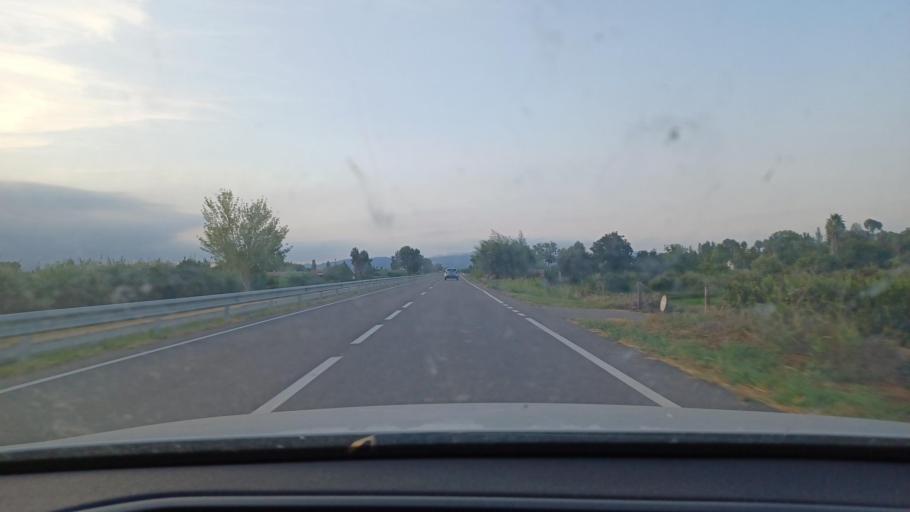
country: ES
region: Catalonia
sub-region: Provincia de Tarragona
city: Amposta
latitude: 40.6745
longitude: 0.5906
